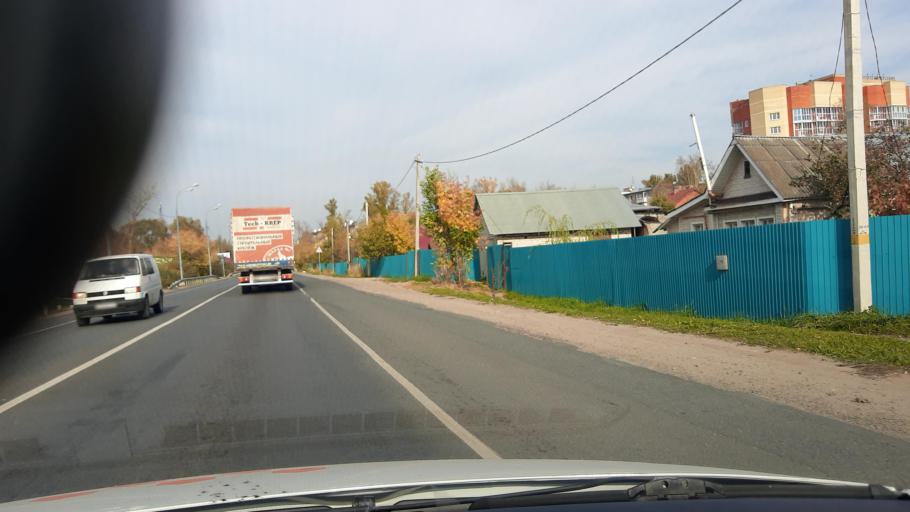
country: RU
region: Moskovskaya
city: Elektrostal'
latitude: 55.7859
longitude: 38.4315
